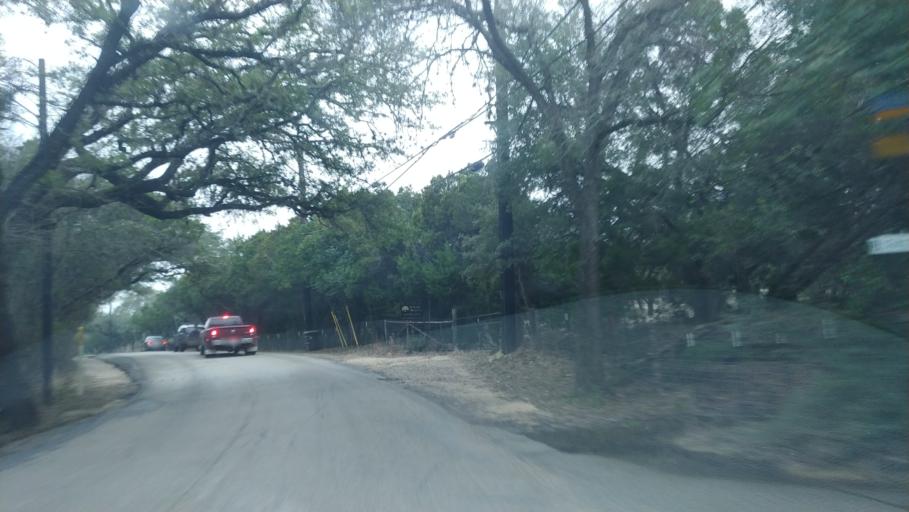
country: US
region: Texas
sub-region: Bexar County
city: Cross Mountain
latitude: 29.6218
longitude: -98.6848
